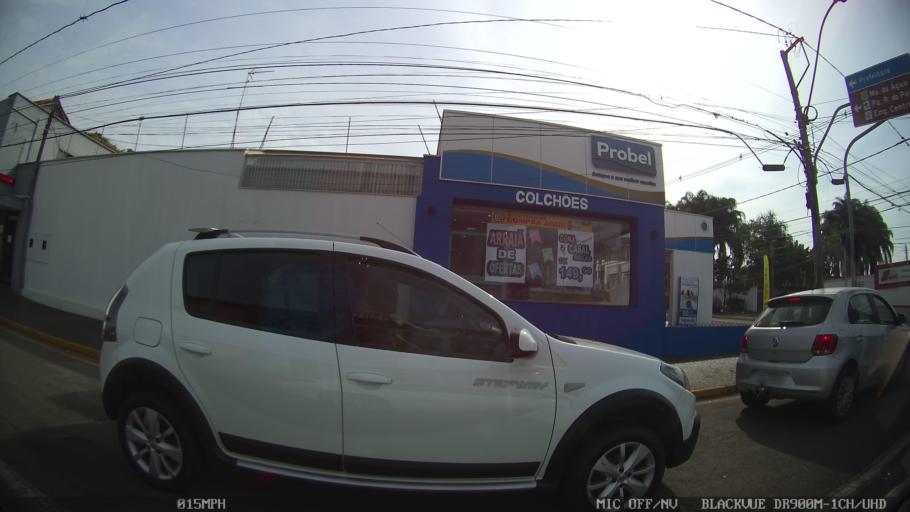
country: BR
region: Sao Paulo
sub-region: Piracicaba
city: Piracicaba
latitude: -22.7348
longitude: -47.6499
